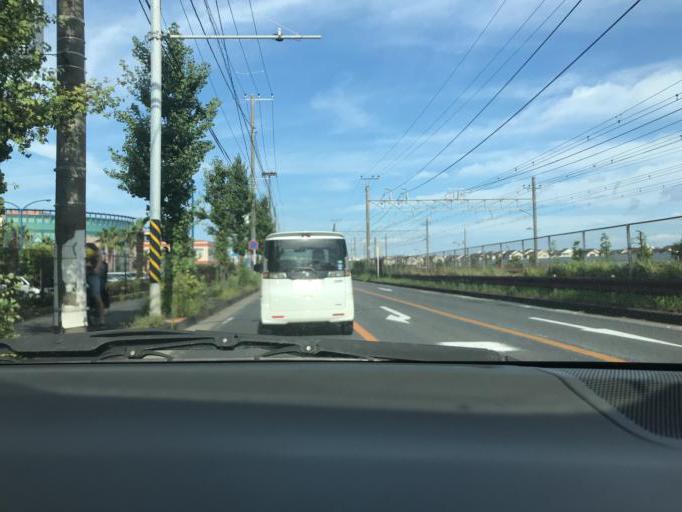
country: JP
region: Kanagawa
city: Fujisawa
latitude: 35.3378
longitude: 139.4632
